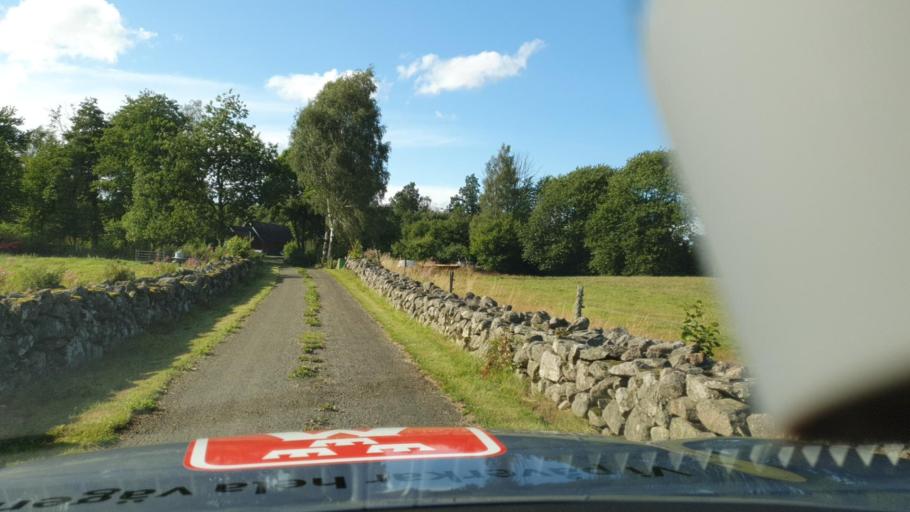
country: SE
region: Skane
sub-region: Hassleholms Kommun
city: Vinslov
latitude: 56.0423
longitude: 13.8685
